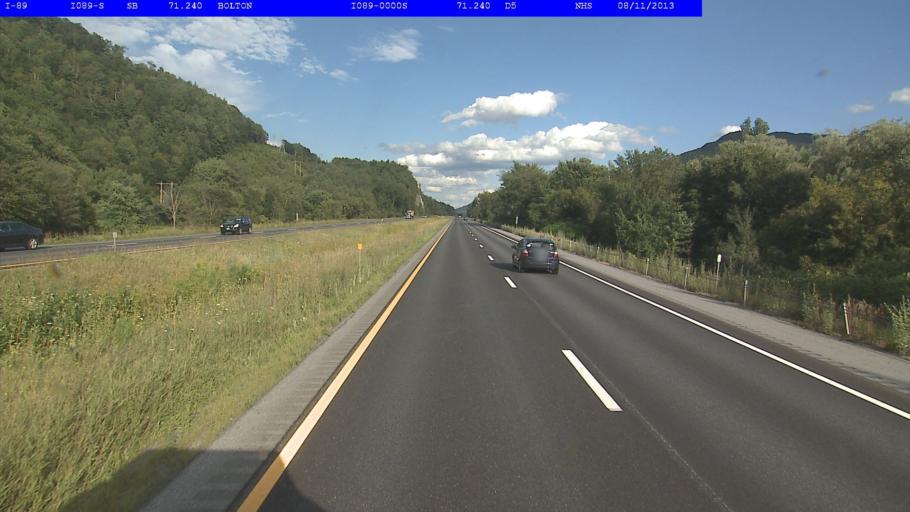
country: US
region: Vermont
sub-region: Washington County
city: Waterbury
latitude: 44.3767
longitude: -72.8916
